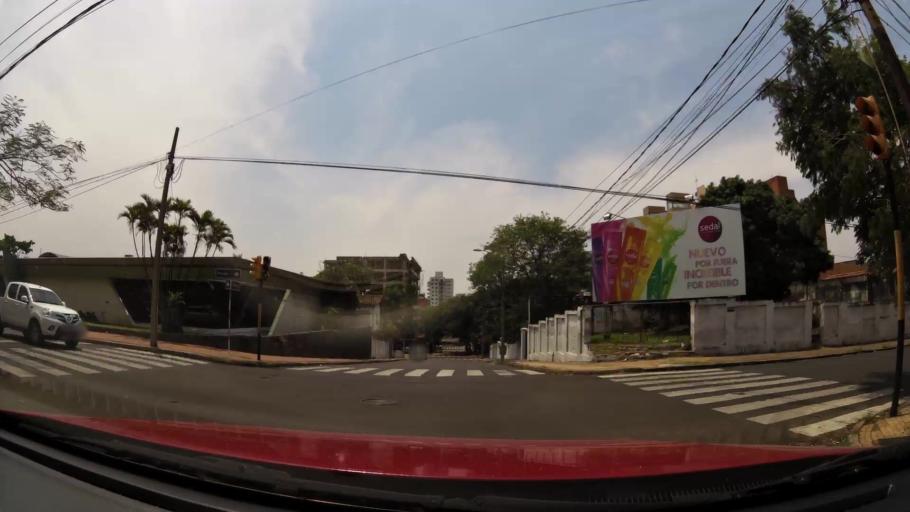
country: PY
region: Asuncion
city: Asuncion
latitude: -25.2932
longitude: -57.6168
